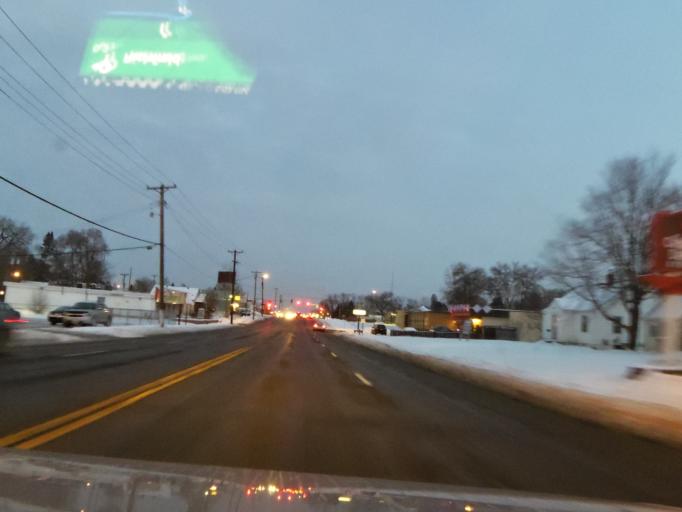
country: US
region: Minnesota
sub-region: Hennepin County
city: Richfield
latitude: 44.8835
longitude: -93.2555
